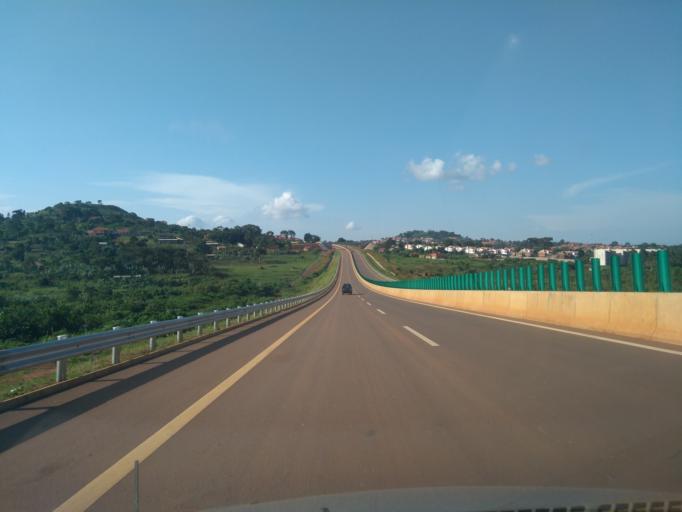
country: UG
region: Central Region
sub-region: Wakiso District
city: Kajansi
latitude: 0.1801
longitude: 32.5200
